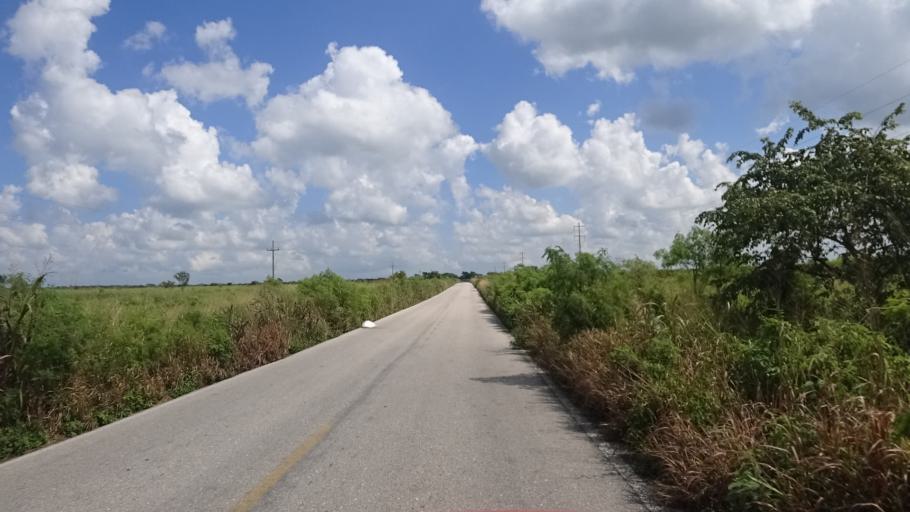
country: MX
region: Yucatan
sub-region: Panaba
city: Loche
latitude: 21.3589
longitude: -88.1465
